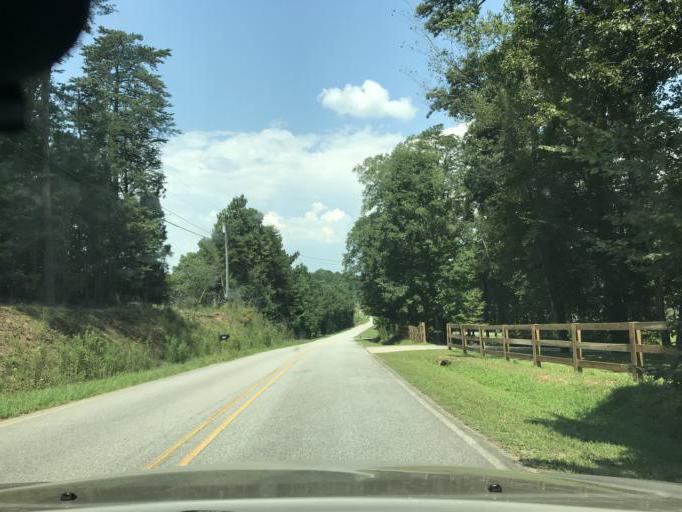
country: US
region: Georgia
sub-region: Dawson County
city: Dawsonville
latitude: 34.3459
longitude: -84.0855
